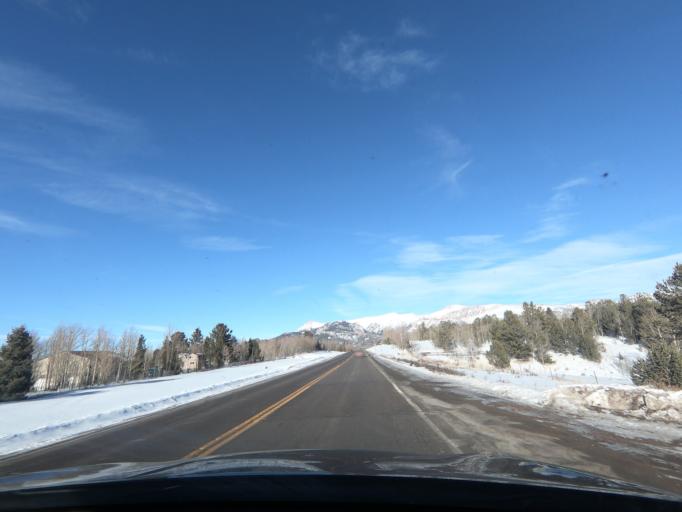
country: US
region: Colorado
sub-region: Teller County
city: Cripple Creek
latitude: 38.7752
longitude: -105.1477
